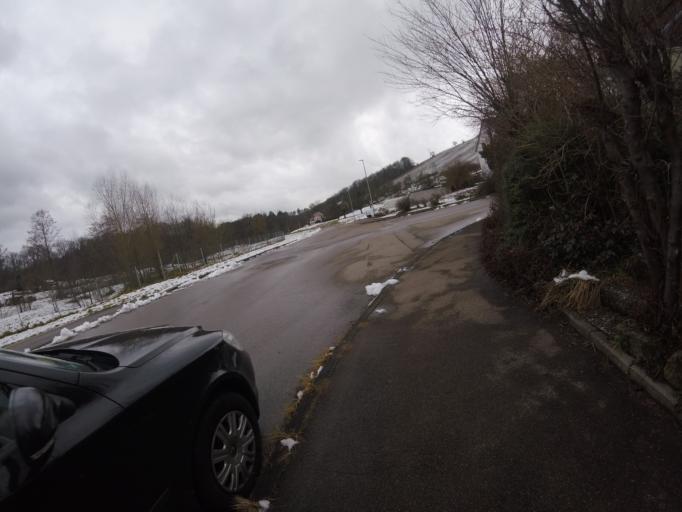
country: DE
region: Baden-Wuerttemberg
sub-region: Regierungsbezirk Stuttgart
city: Oberstenfeld
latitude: 48.9942
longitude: 9.3507
